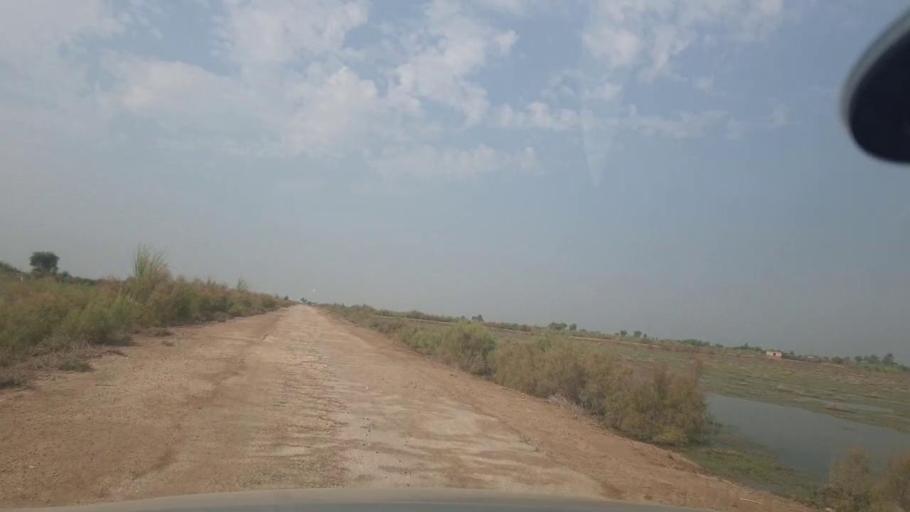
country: PK
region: Balochistan
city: Mehrabpur
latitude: 28.0215
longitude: 68.1394
